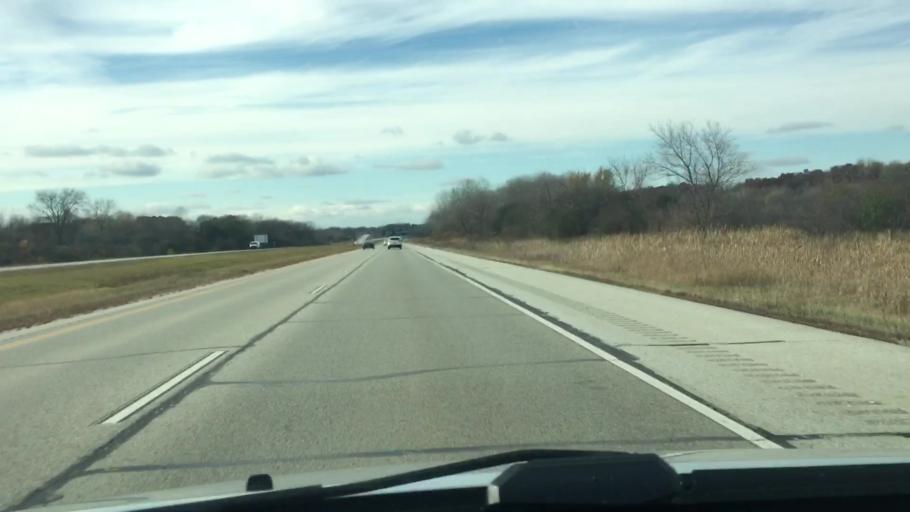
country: US
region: Wisconsin
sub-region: Waukesha County
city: Pewaukee
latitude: 43.1002
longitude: -88.2953
